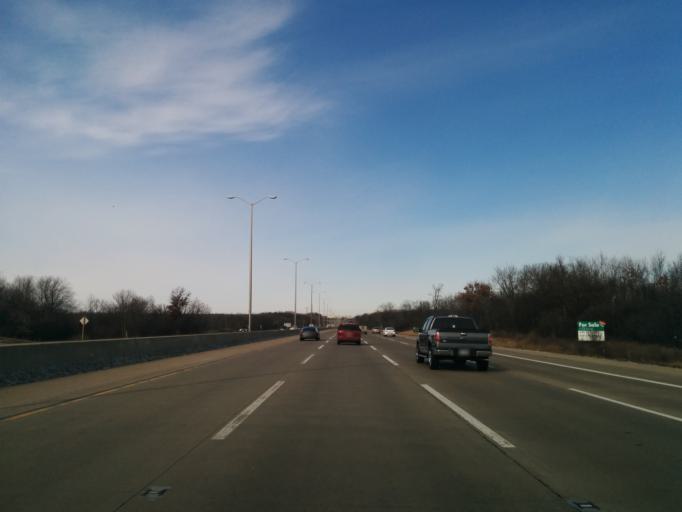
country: US
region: Illinois
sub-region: Lake County
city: Gurnee
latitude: 42.3462
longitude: -87.9239
